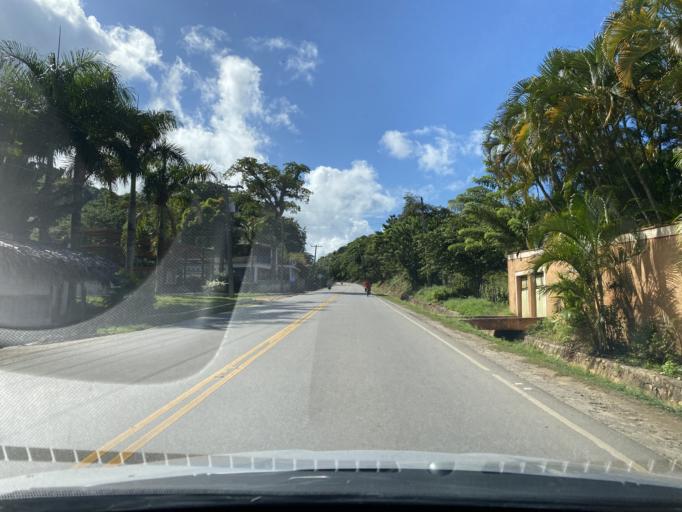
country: DO
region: Samana
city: Las Terrenas
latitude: 19.3110
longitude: -69.5303
